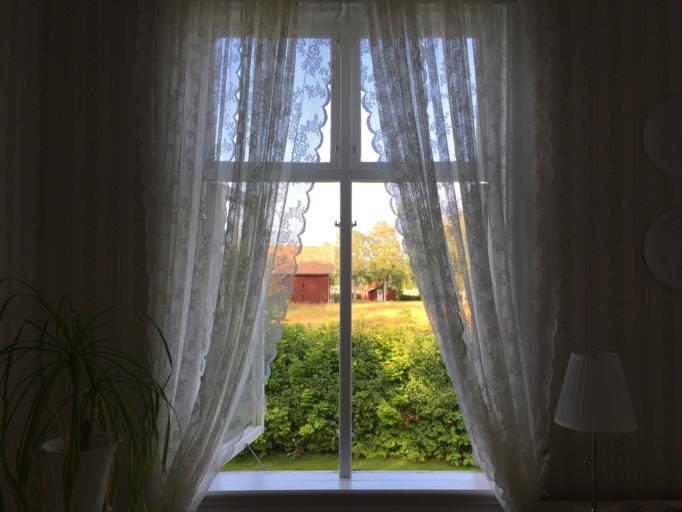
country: SE
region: Dalarna
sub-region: Ludvika Kommun
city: Grangesberg
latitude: 60.2593
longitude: 14.9791
